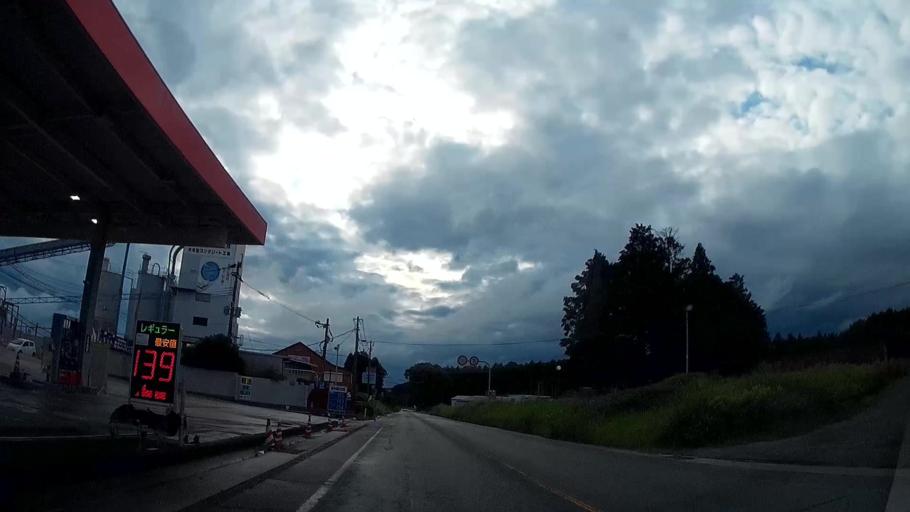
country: JP
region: Kumamoto
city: Ozu
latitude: 32.8789
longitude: 130.9121
